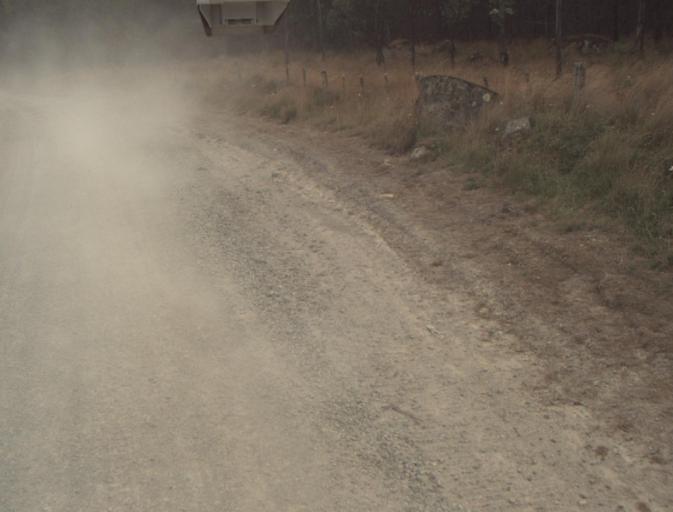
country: AU
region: Tasmania
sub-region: Dorset
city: Scottsdale
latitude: -41.3498
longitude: 147.4493
